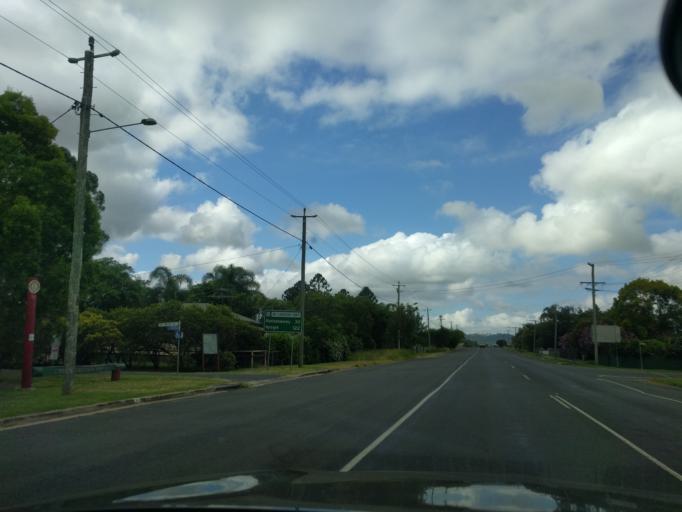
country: AU
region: Queensland
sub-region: Logan
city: Cedar Vale
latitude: -27.9924
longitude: 152.9921
